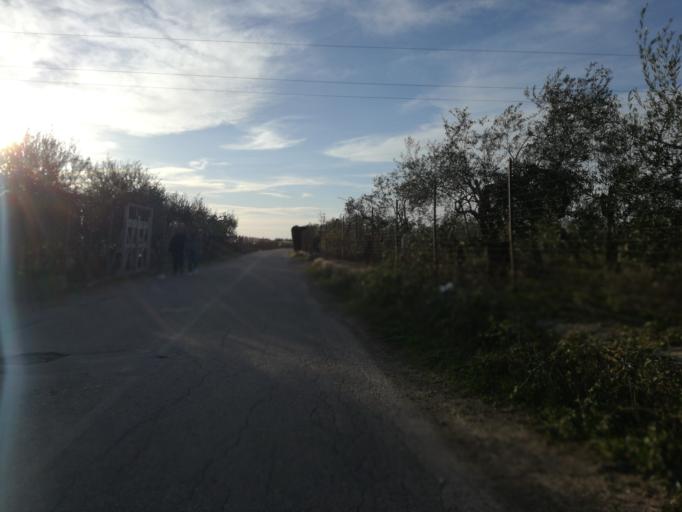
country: IT
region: Apulia
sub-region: Provincia di Bari
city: Capurso
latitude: 41.0502
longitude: 16.9042
